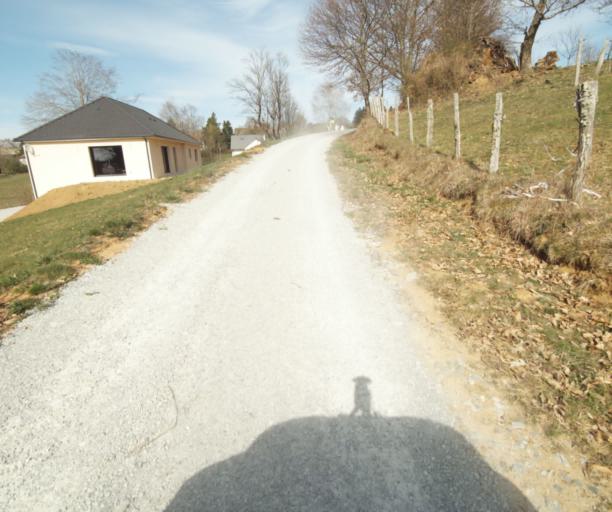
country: FR
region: Limousin
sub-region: Departement de la Correze
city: Naves
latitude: 45.3384
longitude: 1.7455
